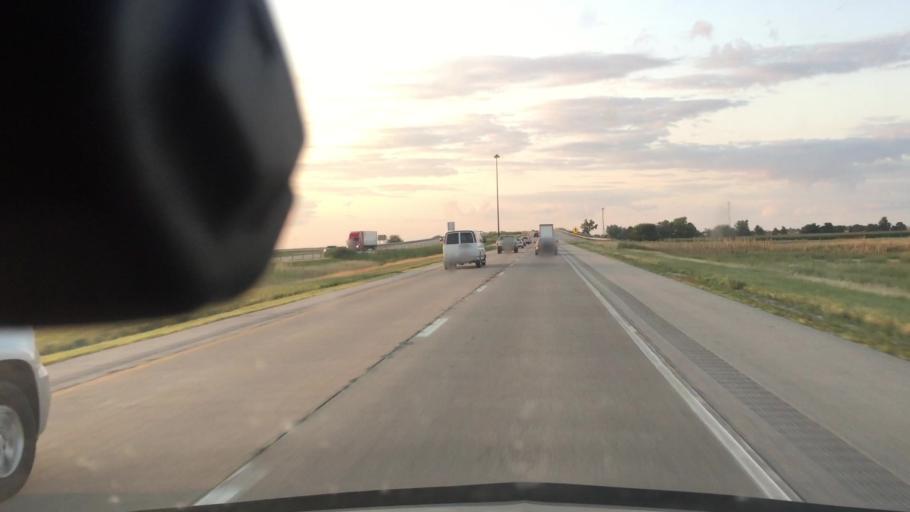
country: US
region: Illinois
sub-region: Livingston County
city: Dwight
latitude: 41.0949
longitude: -88.4502
